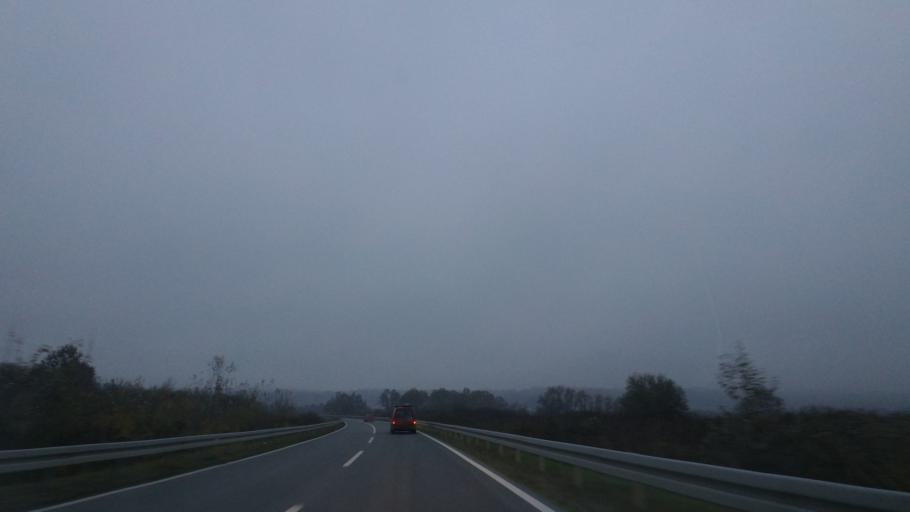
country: HR
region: Sisacko-Moslavacka
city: Petrinja
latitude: 45.4464
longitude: 16.2592
